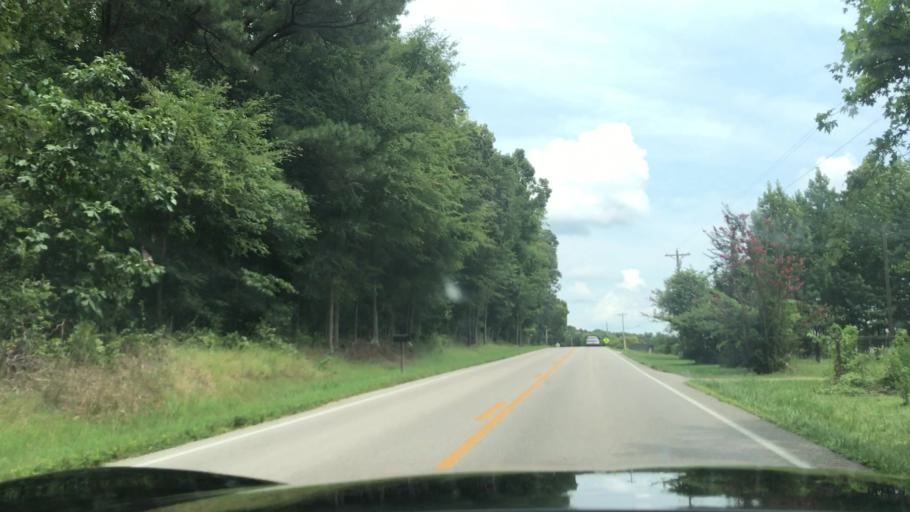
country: US
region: Kentucky
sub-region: Butler County
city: Morgantown
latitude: 37.1731
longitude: -86.8131
